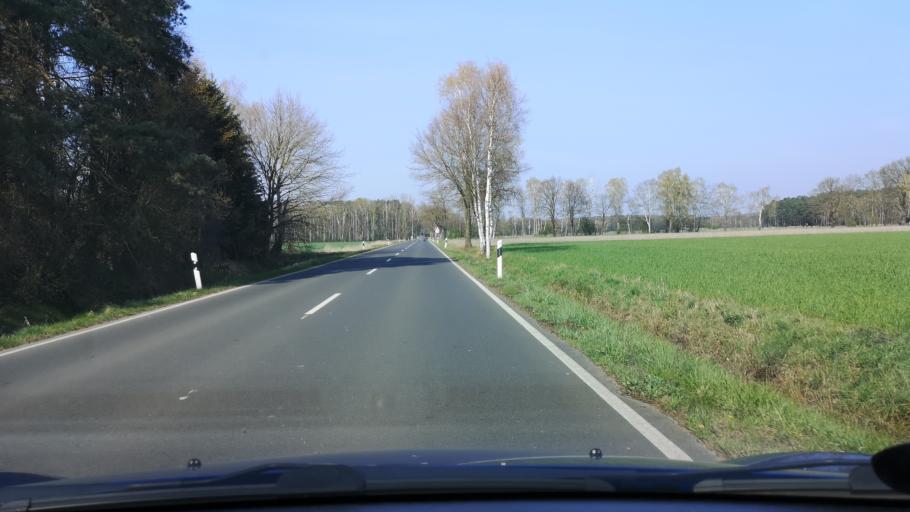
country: DE
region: Lower Saxony
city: Neustadt am Rubenberge
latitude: 52.4832
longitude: 9.5366
